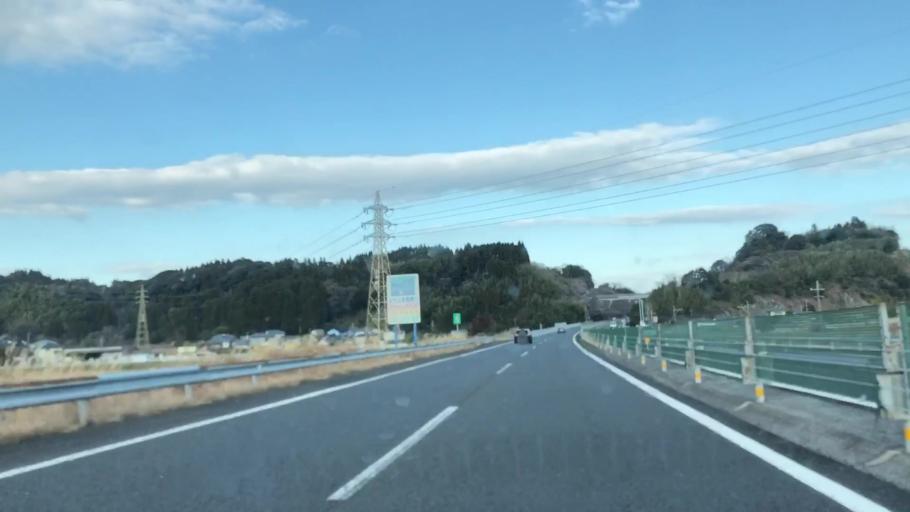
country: JP
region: Miyazaki
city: Miyazaki-shi
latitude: 31.8617
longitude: 131.3803
